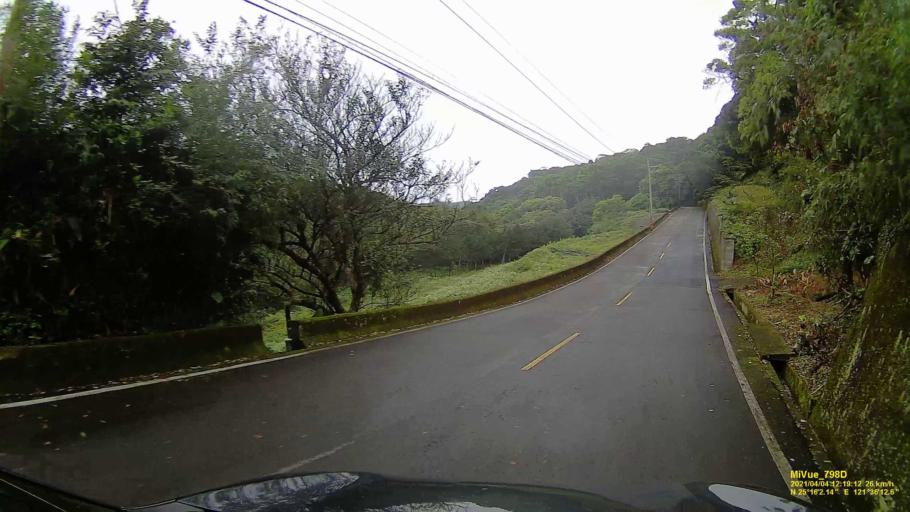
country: TW
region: Taiwan
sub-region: Keelung
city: Keelung
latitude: 25.2674
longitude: 121.6035
